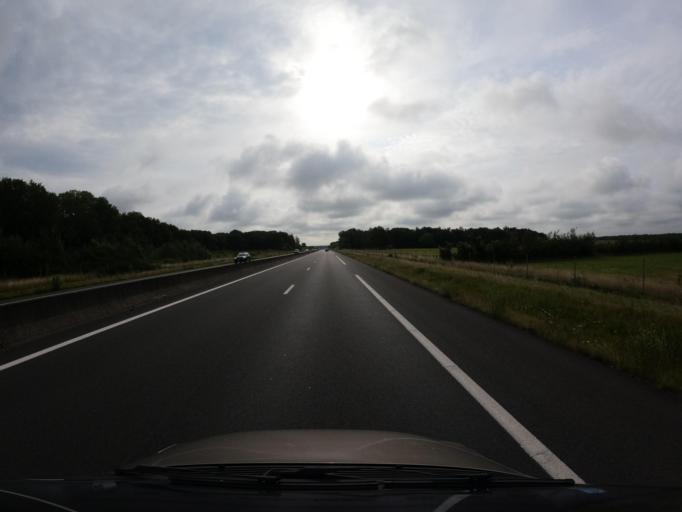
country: FR
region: Centre
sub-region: Departement d'Indre-et-Loire
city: Ballan-Mire
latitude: 47.3076
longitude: 0.6096
